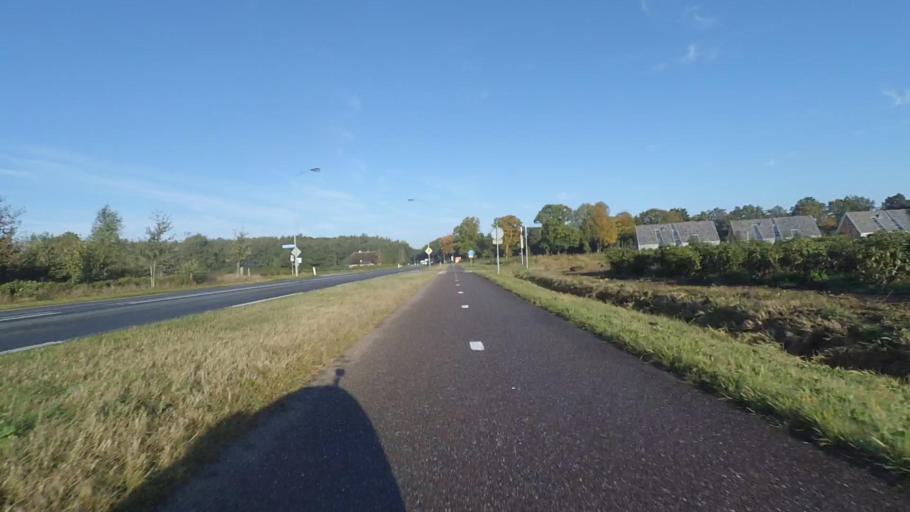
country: NL
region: Gelderland
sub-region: Gemeente Apeldoorn
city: Uddel
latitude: 52.2400
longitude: 5.7637
